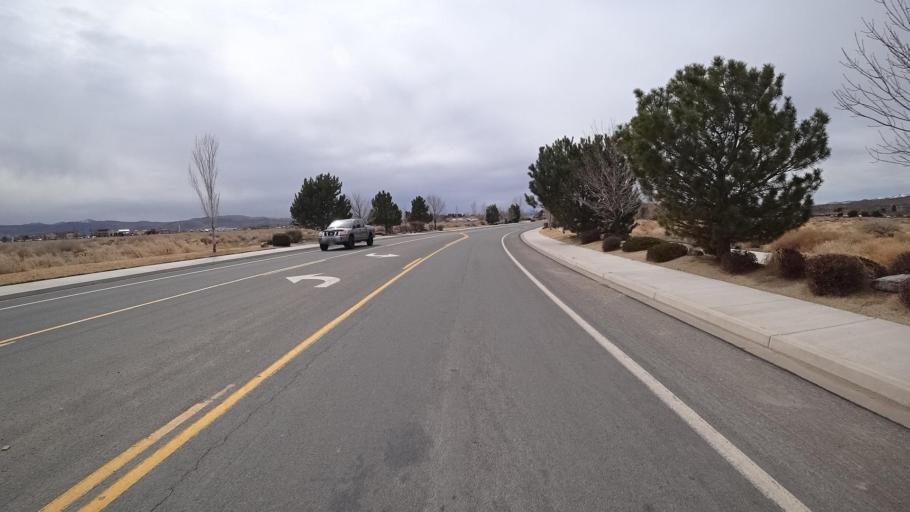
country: US
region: Nevada
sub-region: Washoe County
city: Spanish Springs
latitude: 39.6433
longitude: -119.7174
